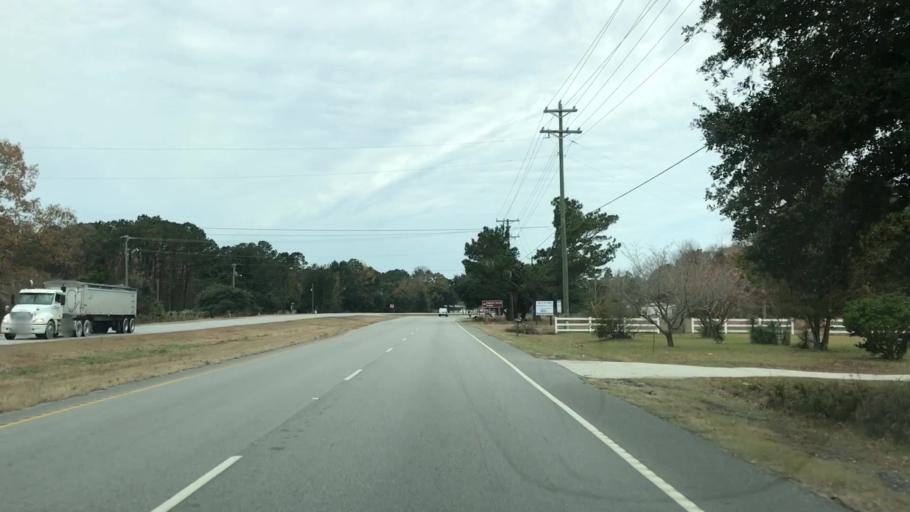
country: US
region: South Carolina
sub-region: Charleston County
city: Isle of Palms
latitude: 32.8857
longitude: -79.7472
